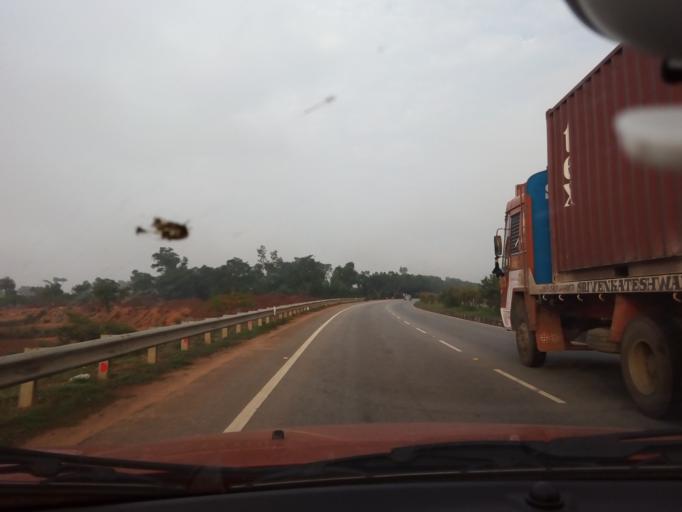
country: IN
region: Karnataka
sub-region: Ramanagara
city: Magadi
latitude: 13.0481
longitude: 77.1454
